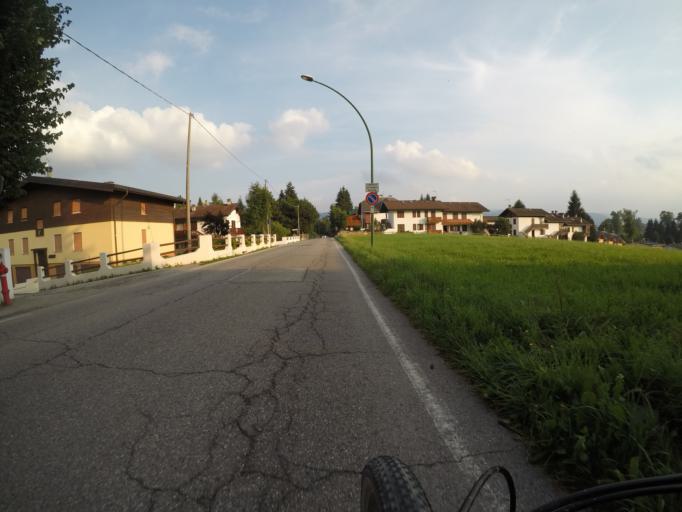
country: IT
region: Veneto
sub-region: Provincia di Vicenza
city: Asiago
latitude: 45.8813
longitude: 11.5050
